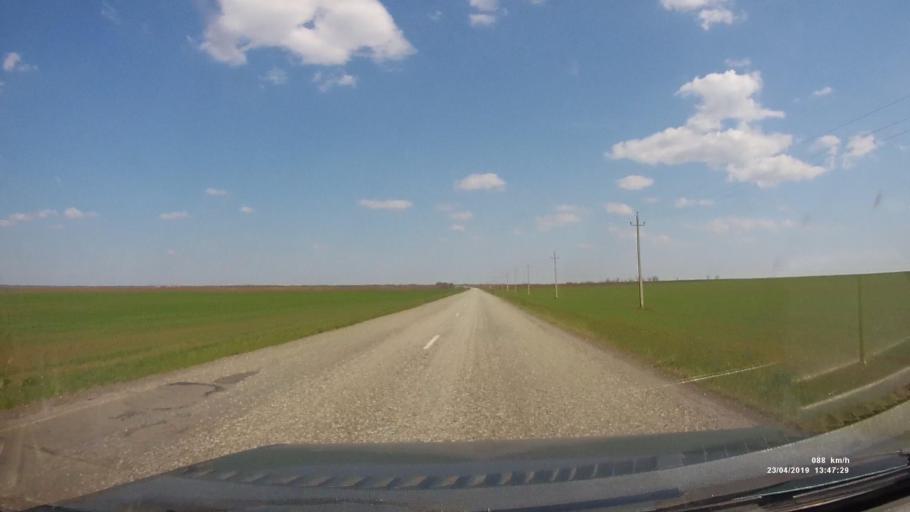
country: RU
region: Kalmykiya
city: Yashalta
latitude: 46.5994
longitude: 42.8548
